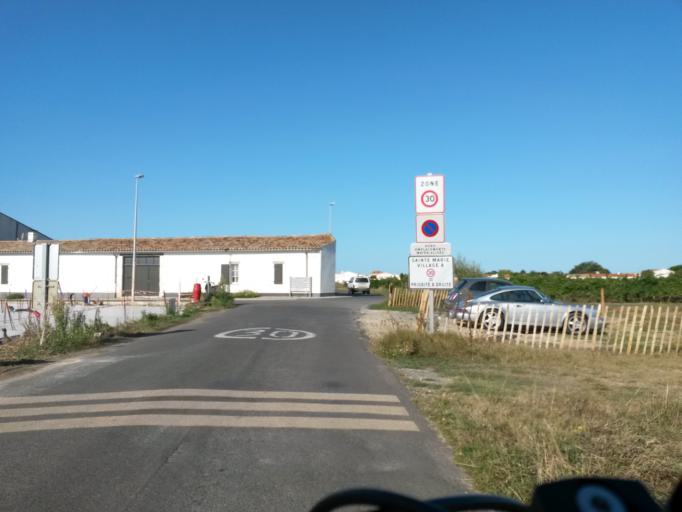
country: FR
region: Poitou-Charentes
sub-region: Departement de la Charente-Maritime
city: Sainte-Marie-de-Re
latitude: 46.1515
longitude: -1.3036
